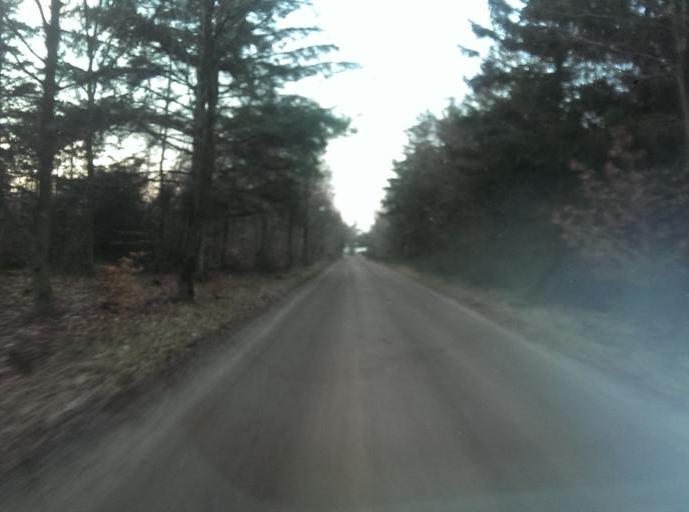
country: DK
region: South Denmark
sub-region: Varde Kommune
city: Oksbol
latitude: 55.5650
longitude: 8.3114
